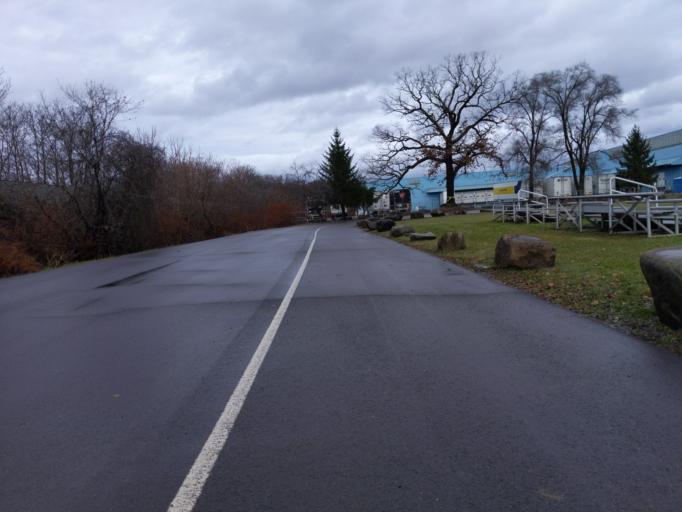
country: US
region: New York
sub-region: Chemung County
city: Elmira Heights
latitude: 42.1164
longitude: -76.8205
